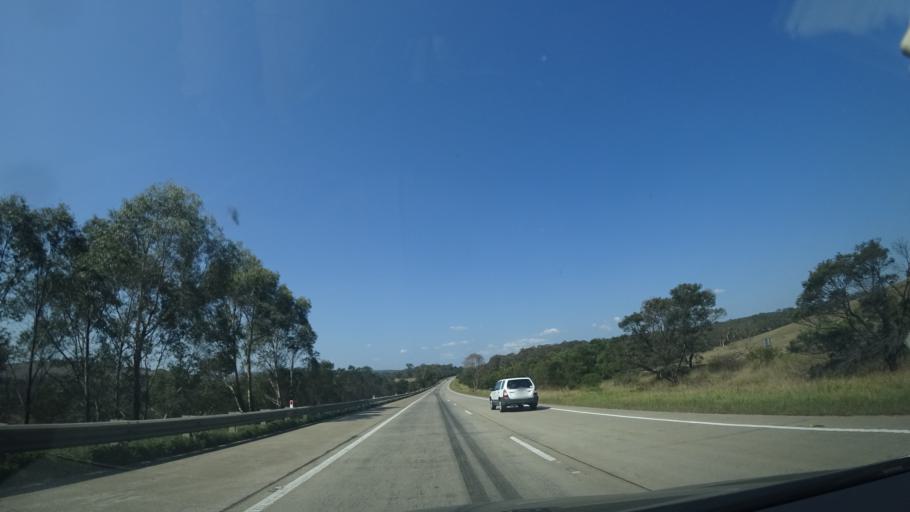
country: AU
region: New South Wales
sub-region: Wingecarribee
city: Bowral
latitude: -34.4519
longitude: 150.3688
